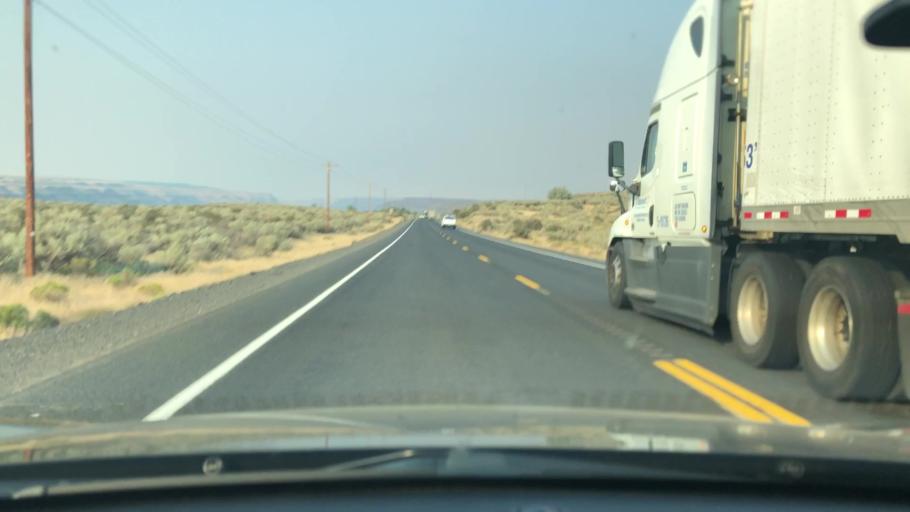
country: US
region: Oregon
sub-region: Umatilla County
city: Stanfield
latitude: 45.9179
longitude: -119.1290
